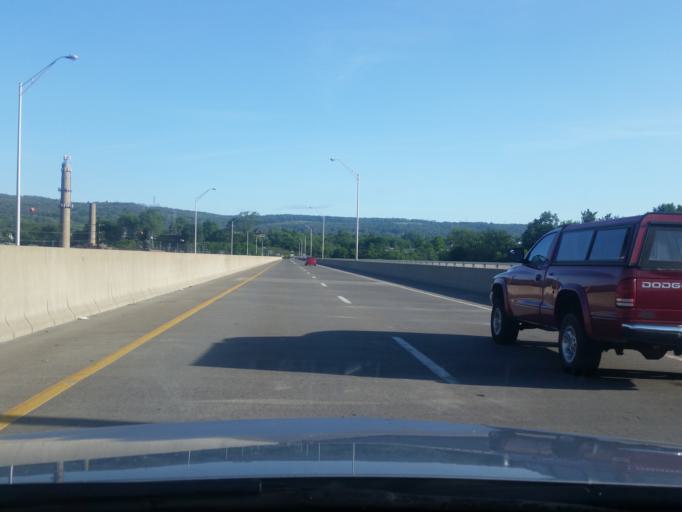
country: US
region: Pennsylvania
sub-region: Luzerne County
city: Larksville
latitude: 41.2392
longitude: -75.9308
